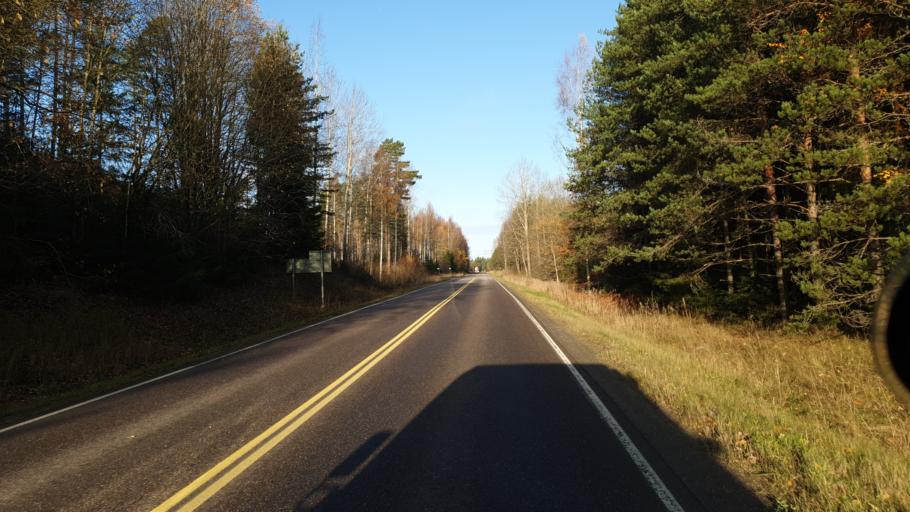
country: FI
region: Uusimaa
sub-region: Helsinki
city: Siuntio
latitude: 60.1925
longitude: 24.1999
